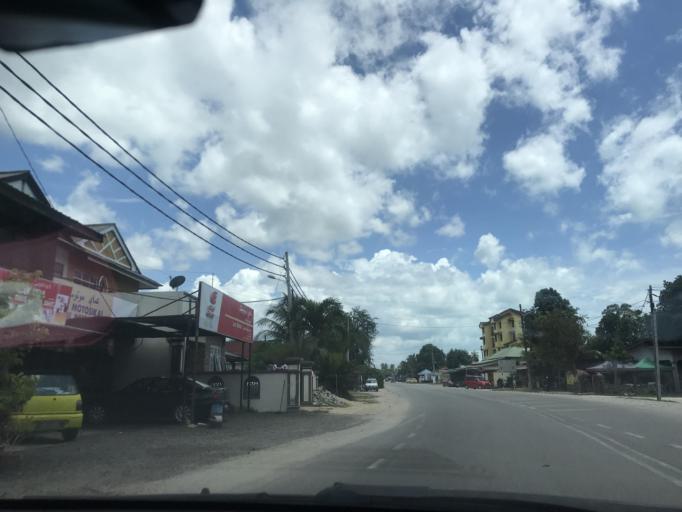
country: TH
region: Narathiwat
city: Tak Bai
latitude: 6.2244
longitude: 102.1052
